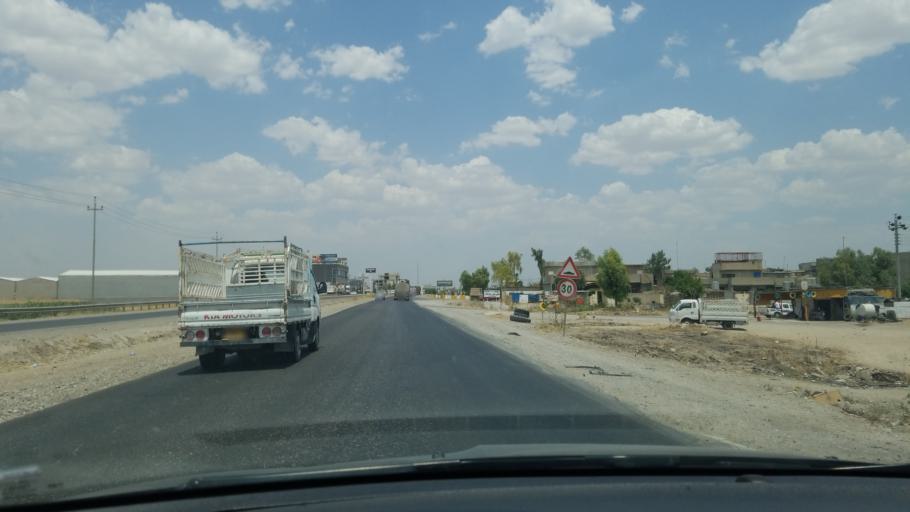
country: IQ
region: Arbil
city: Erbil
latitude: 36.0972
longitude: 44.0215
